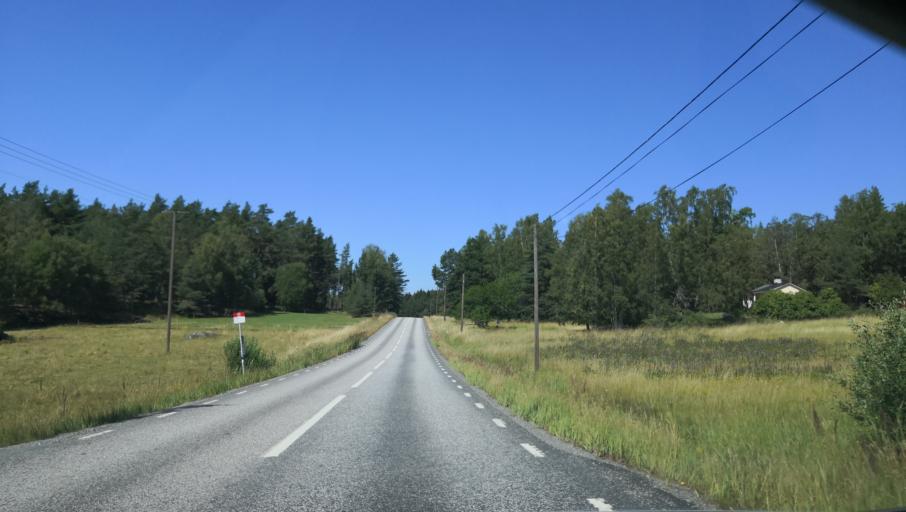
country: SE
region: Stockholm
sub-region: Varmdo Kommun
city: Hemmesta
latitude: 59.3938
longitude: 18.4851
